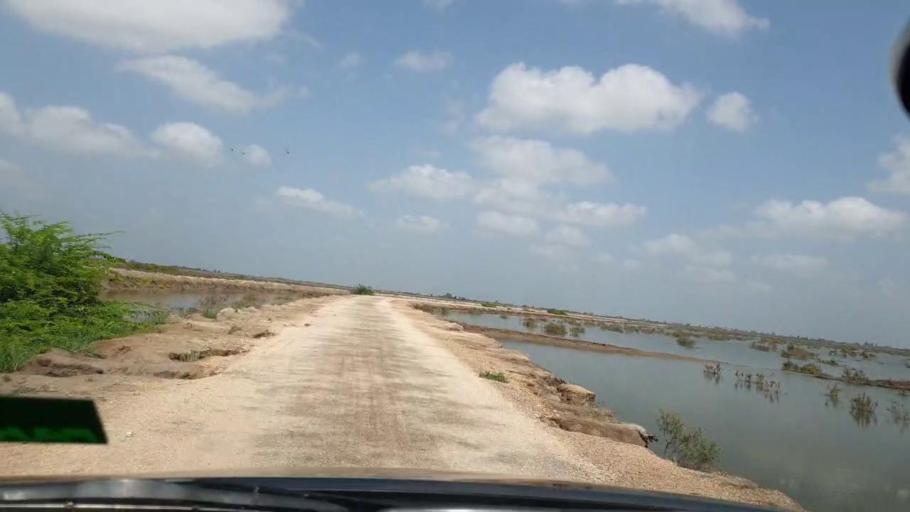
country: PK
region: Sindh
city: Kadhan
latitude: 24.5820
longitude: 69.1401
